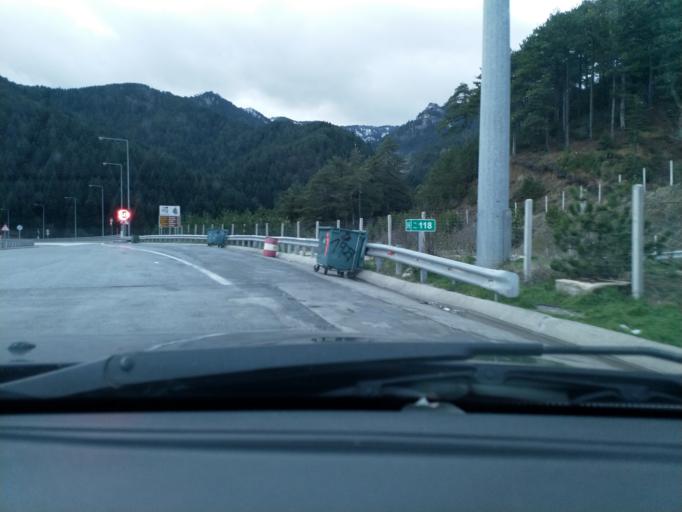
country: GR
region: Epirus
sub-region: Nomos Ioanninon
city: Metsovo
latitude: 39.7900
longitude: 21.2657
